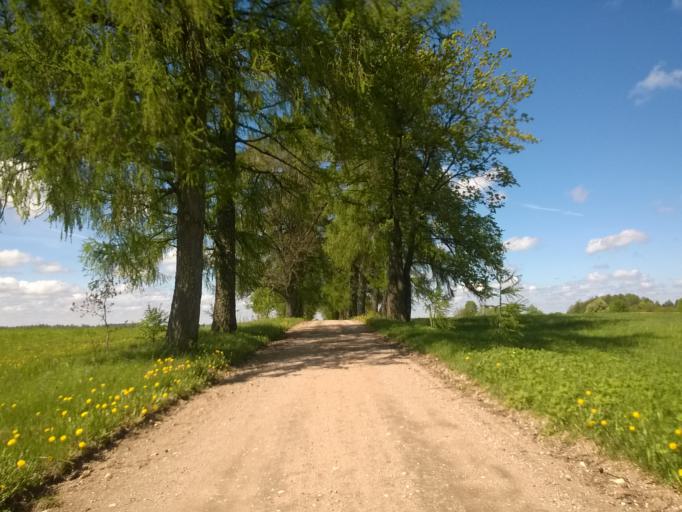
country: LV
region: Amatas Novads
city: Drabesi
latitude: 57.2461
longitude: 25.2752
